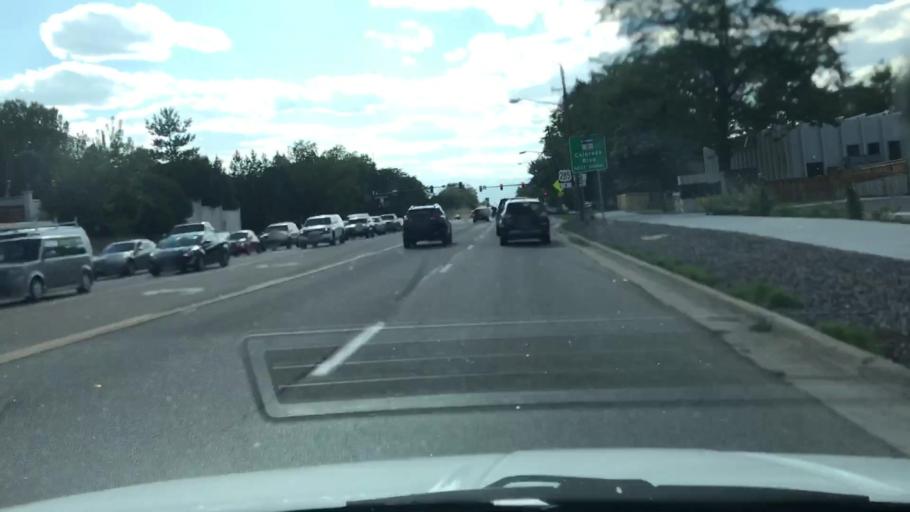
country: US
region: Colorado
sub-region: Arapahoe County
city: Cherry Hills Village
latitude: 39.6531
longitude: -104.9387
